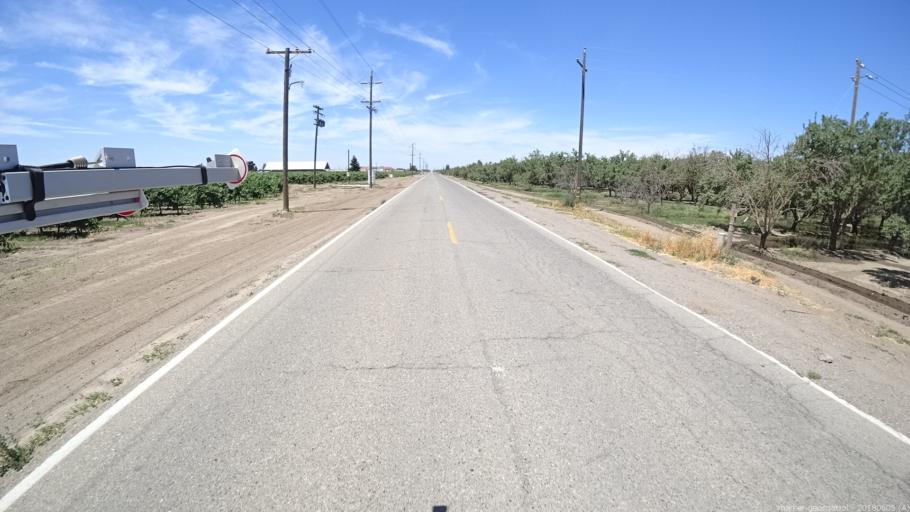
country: US
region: California
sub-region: Merced County
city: Dos Palos
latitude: 37.0752
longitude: -120.4735
